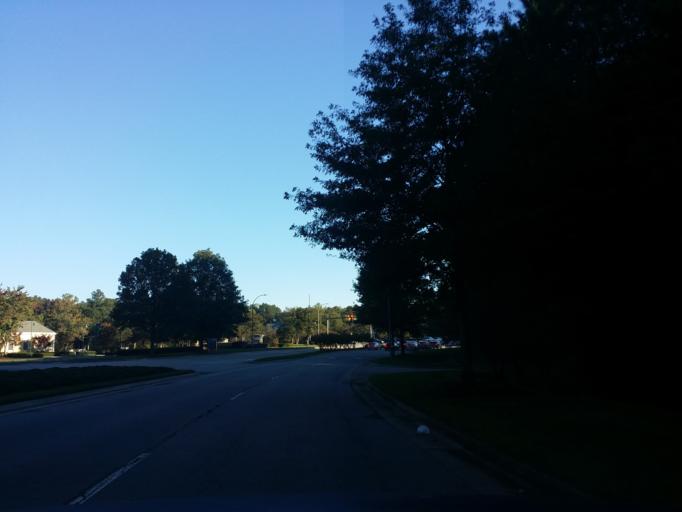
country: US
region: North Carolina
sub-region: Wake County
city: Morrisville
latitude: 35.8251
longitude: -78.8068
